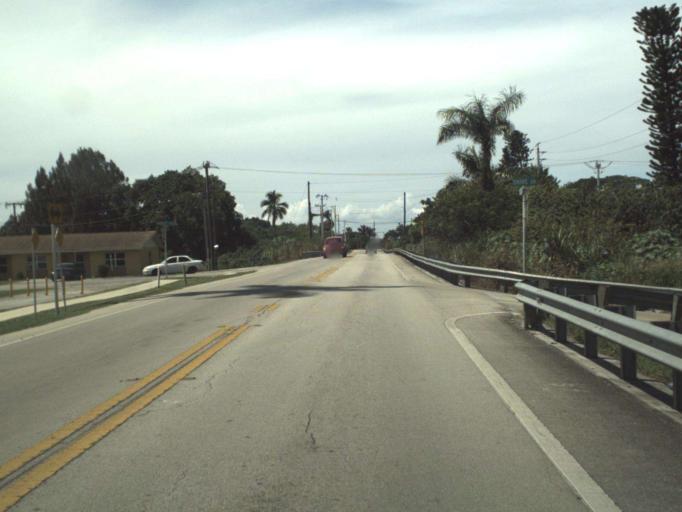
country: US
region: Florida
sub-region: Palm Beach County
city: Pahokee
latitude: 26.8129
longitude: -80.6600
